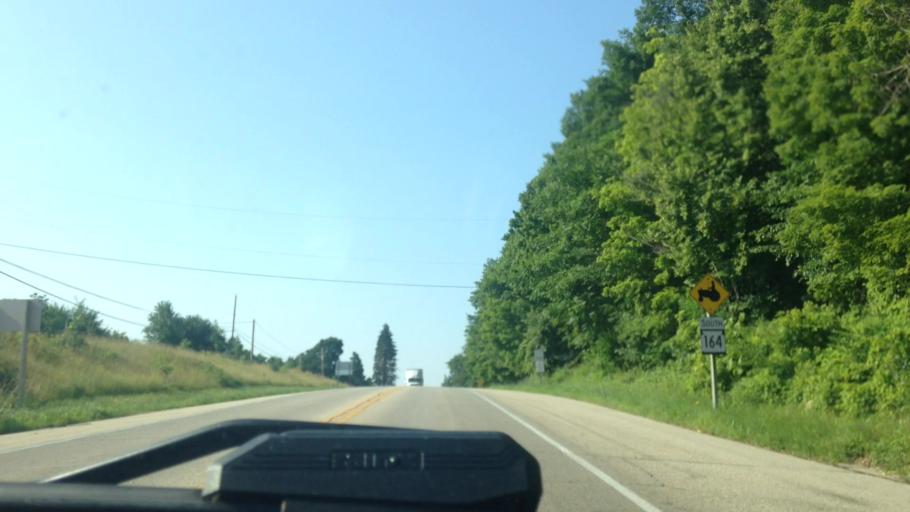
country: US
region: Wisconsin
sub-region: Washington County
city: Richfield
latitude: 43.2505
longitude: -88.2618
